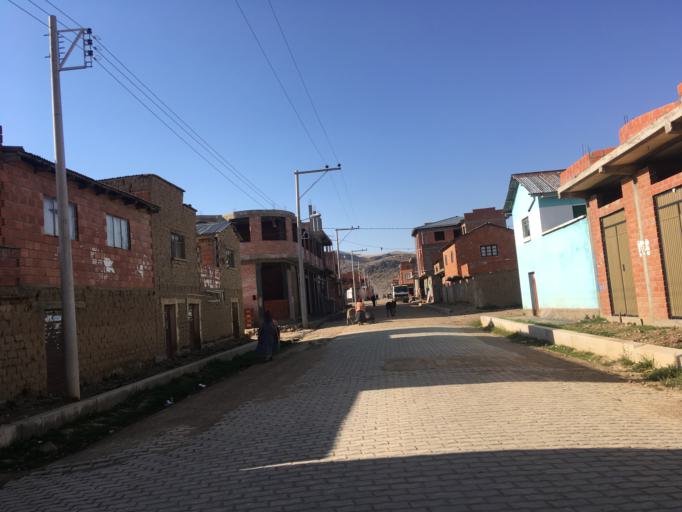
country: BO
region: La Paz
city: Huatajata
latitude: -16.1913
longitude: -68.7445
